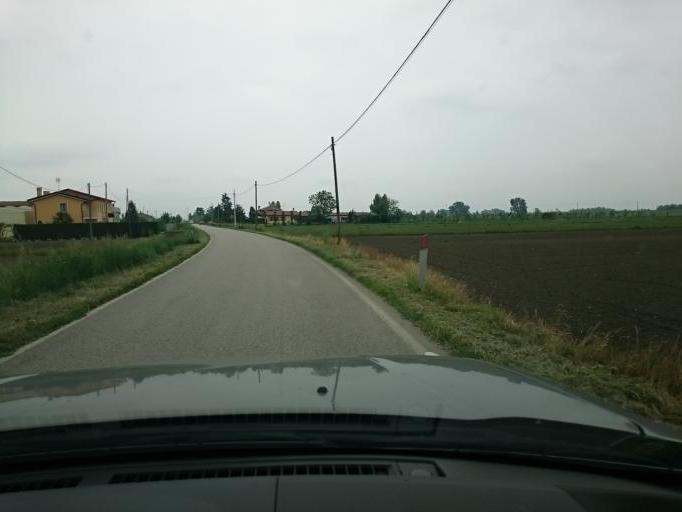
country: IT
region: Veneto
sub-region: Provincia di Padova
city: Bovolenta
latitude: 45.2815
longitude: 11.9138
